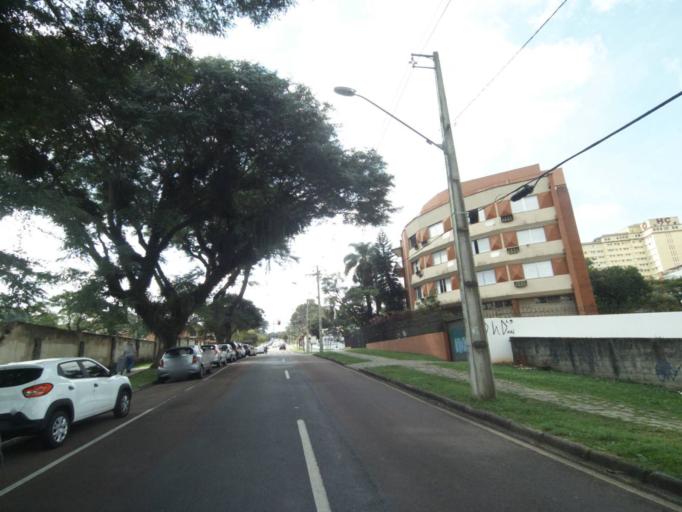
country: BR
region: Parana
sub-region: Curitiba
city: Curitiba
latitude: -25.4241
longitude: -49.2647
